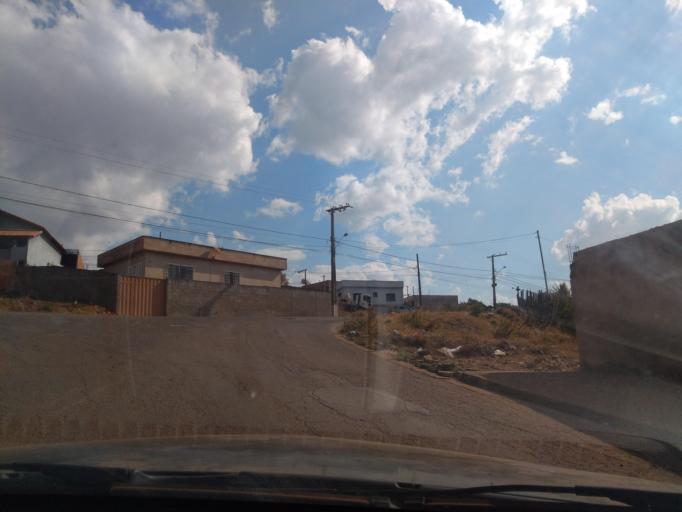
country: BR
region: Minas Gerais
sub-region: Tres Coracoes
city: Tres Coracoes
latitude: -21.6834
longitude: -45.2351
